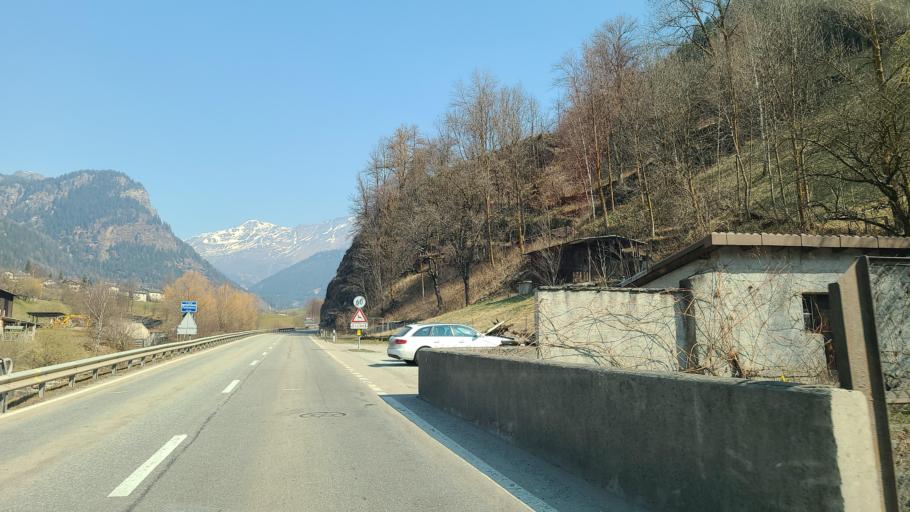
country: CH
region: Grisons
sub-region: Bernina District
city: Poschiavo
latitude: 46.3300
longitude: 10.0586
